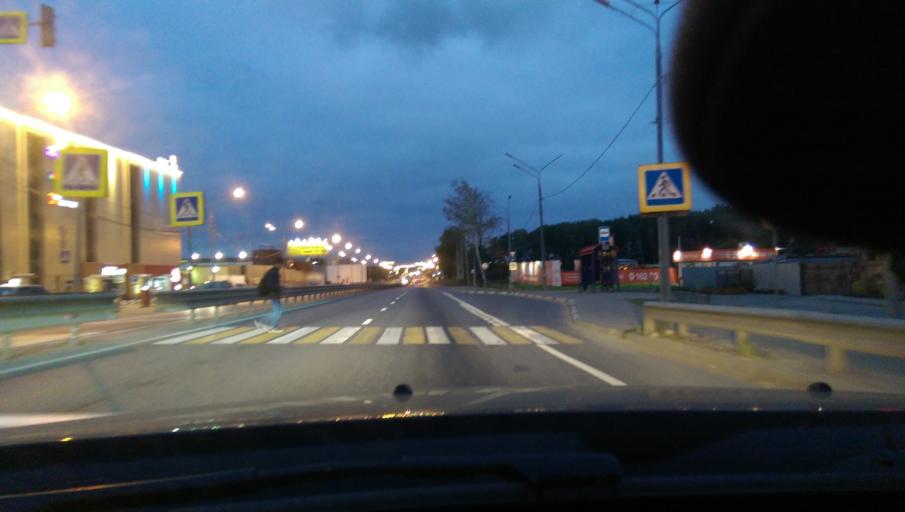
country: RU
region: Moscow
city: Vatutino
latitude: 55.9216
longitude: 37.6638
